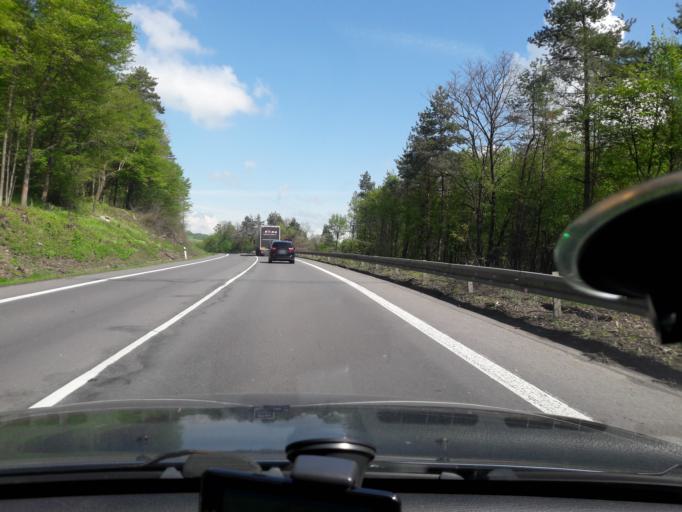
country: SK
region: Banskobystricky
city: Krupina
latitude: 48.4042
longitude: 19.0865
